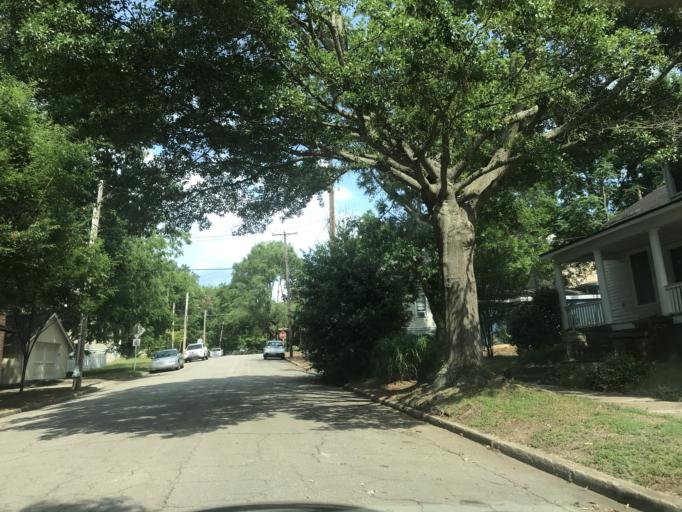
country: US
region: North Carolina
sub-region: Wake County
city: Raleigh
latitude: 35.7757
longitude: -78.6530
